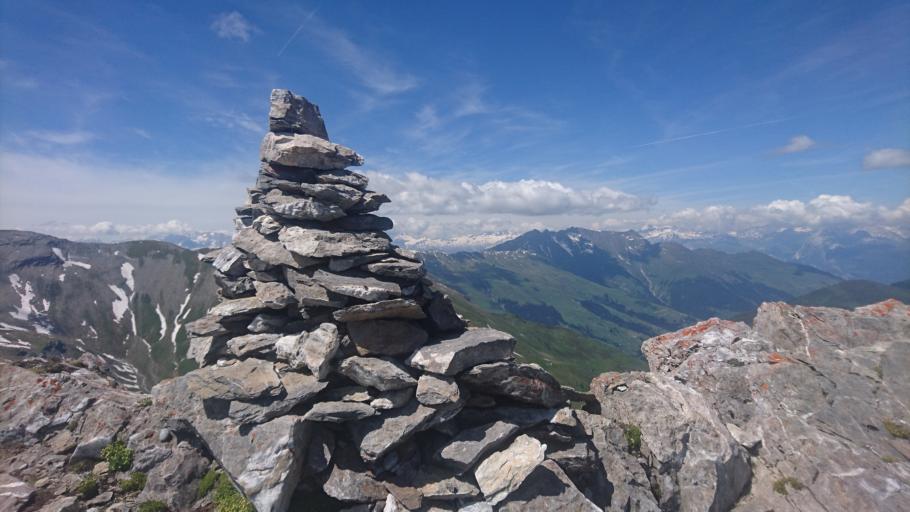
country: CH
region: Grisons
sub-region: Hinterrhein District
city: Thusis
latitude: 46.6347
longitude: 9.3414
